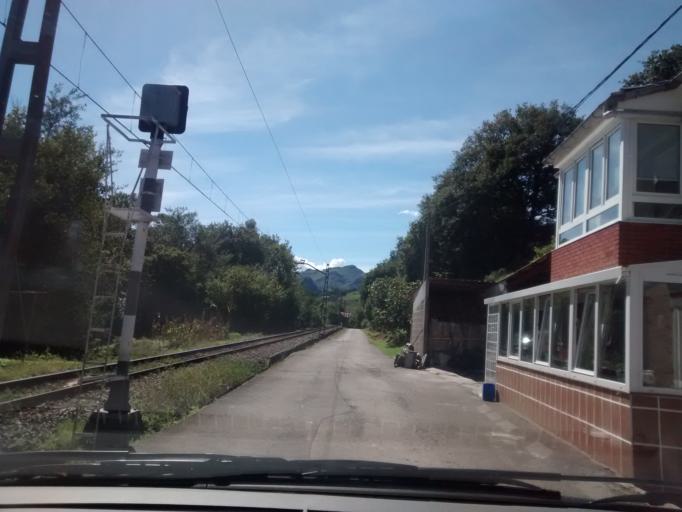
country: ES
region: Cantabria
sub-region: Provincia de Cantabria
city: Entrambasaguas
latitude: 43.3674
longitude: -3.7138
